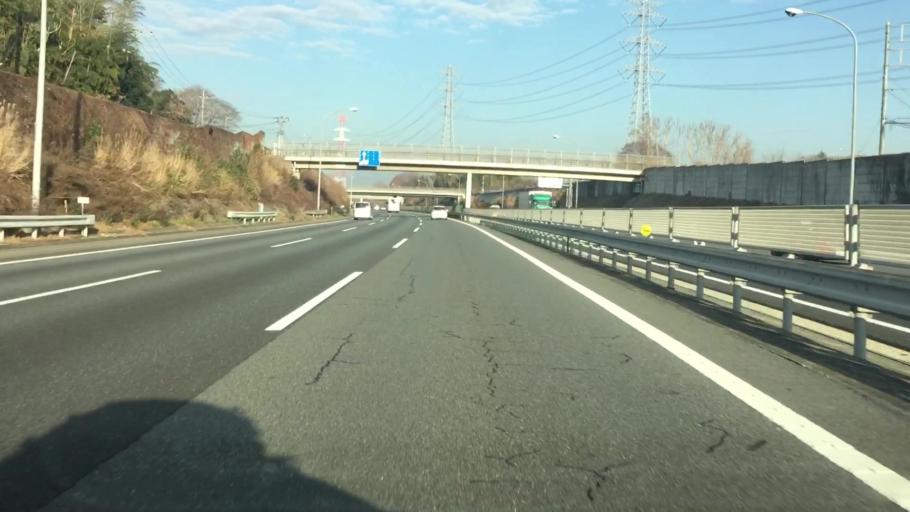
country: JP
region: Saitama
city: Sakado
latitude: 36.0333
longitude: 139.3791
